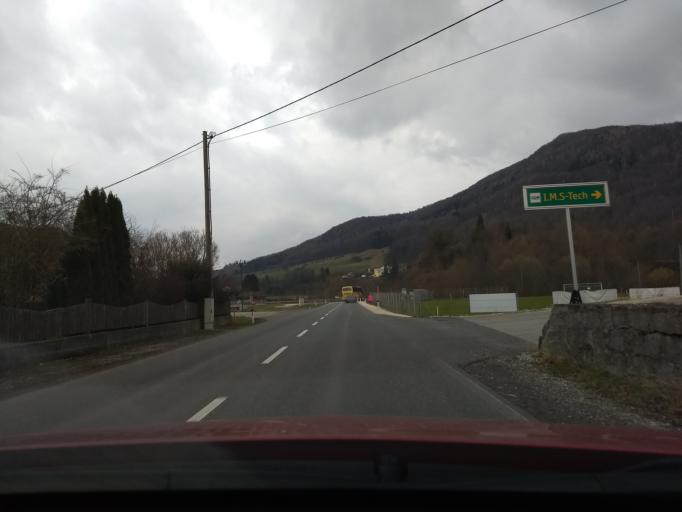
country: AT
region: Upper Austria
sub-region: Politischer Bezirk Steyr-Land
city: Garsten
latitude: 47.9989
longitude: 14.4011
